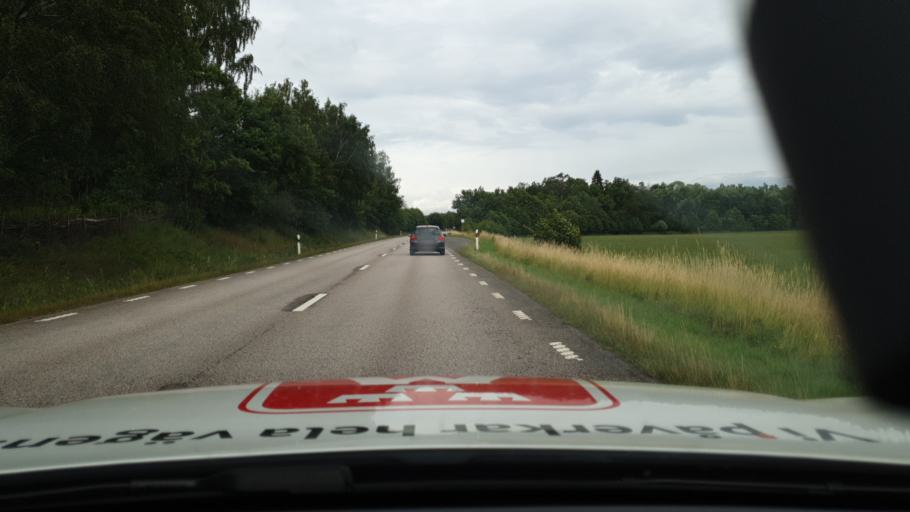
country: SE
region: Vaestra Goetaland
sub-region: Hjo Kommun
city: Hjo
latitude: 58.2066
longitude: 14.2056
